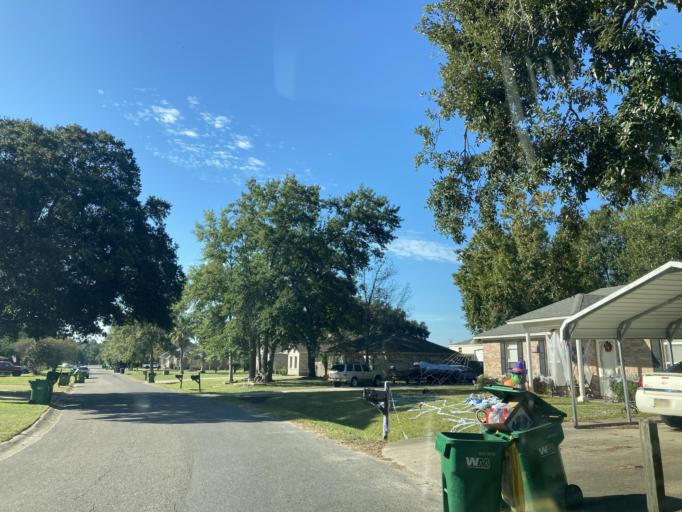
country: US
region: Mississippi
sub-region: Jackson County
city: Saint Martin
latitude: 30.4415
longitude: -88.8797
